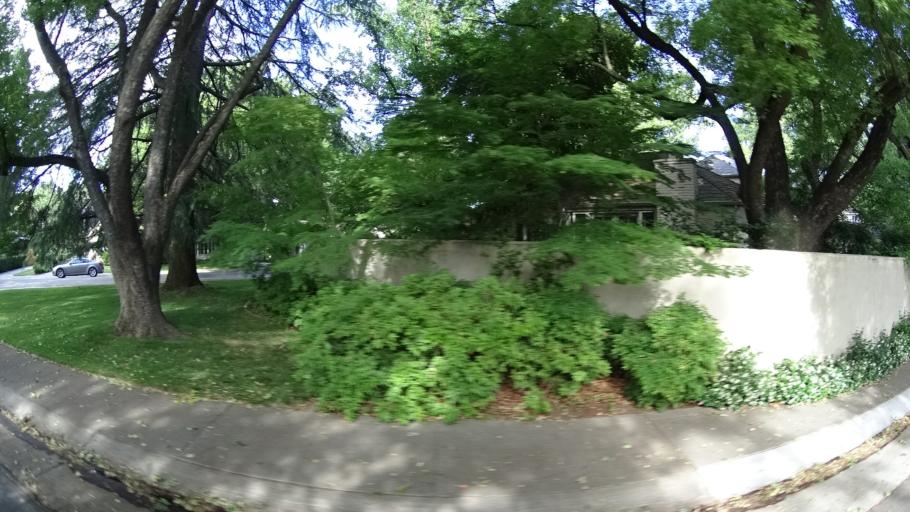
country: US
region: California
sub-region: Sacramento County
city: Sacramento
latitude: 38.5548
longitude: -121.4976
